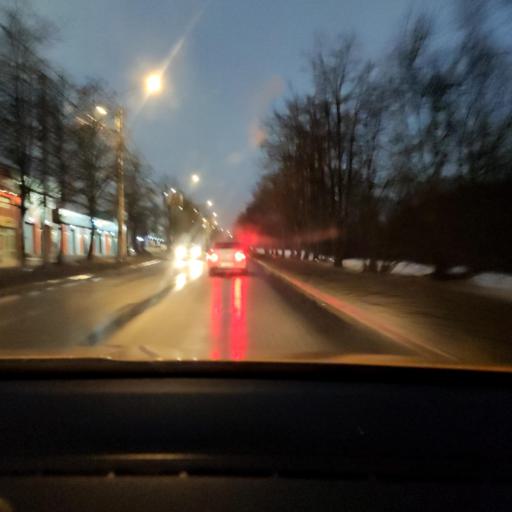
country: RU
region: Moskovskaya
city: Mosrentgen
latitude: 55.6192
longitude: 37.4555
